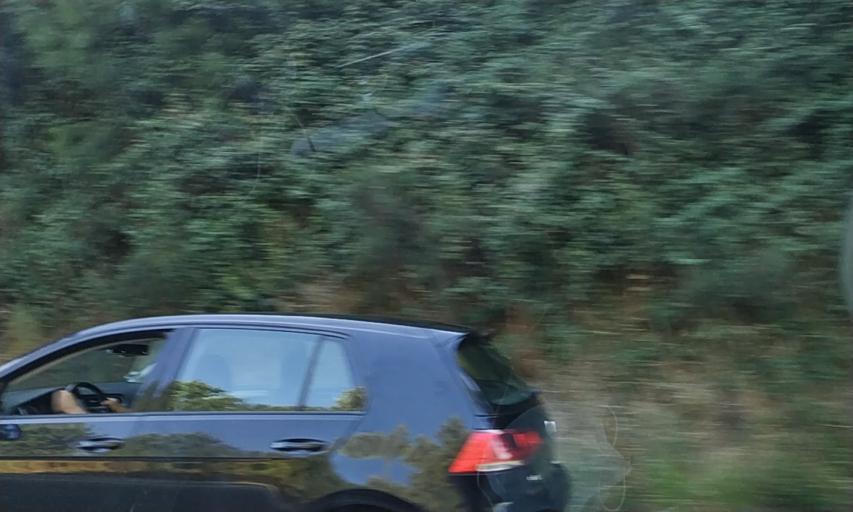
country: PT
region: Porto
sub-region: Santo Tirso
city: Sao Miguel do Couto
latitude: 41.3216
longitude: -8.4690
